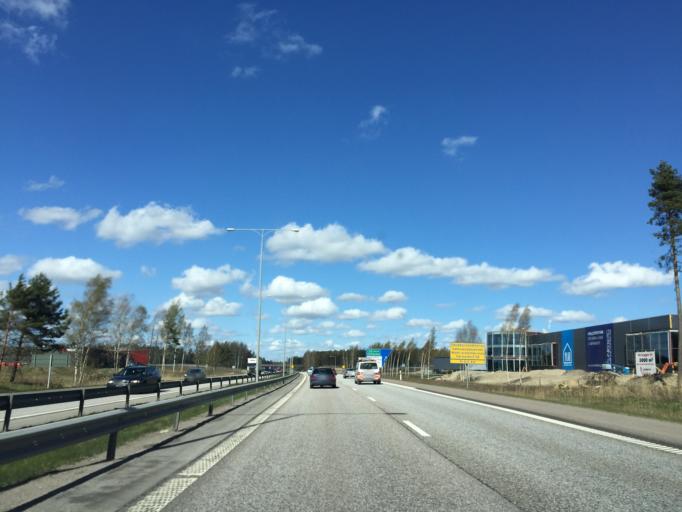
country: SE
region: OErebro
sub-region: Orebro Kommun
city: Orebro
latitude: 59.2341
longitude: 15.1443
